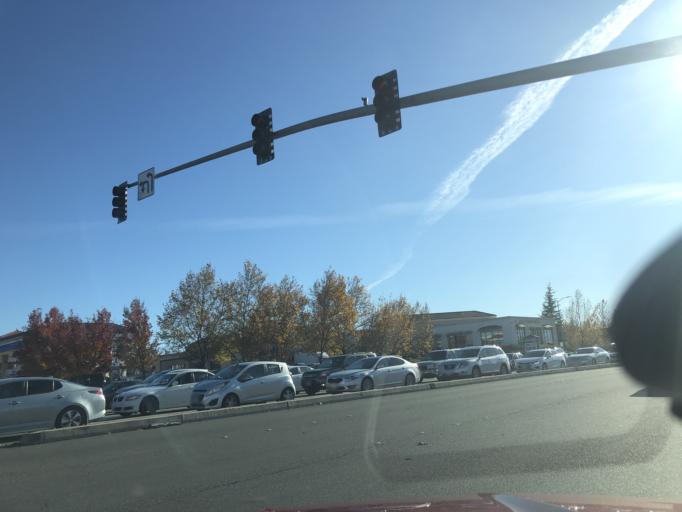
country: US
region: California
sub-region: Placer County
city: Roseville
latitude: 38.7895
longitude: -121.2820
